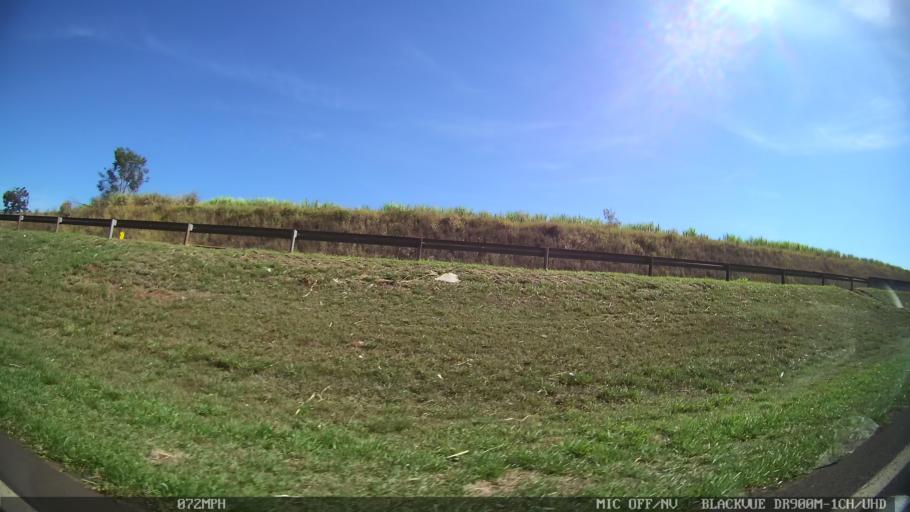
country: BR
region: Sao Paulo
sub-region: Sao Simao
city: Sao Simao
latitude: -21.4985
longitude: -47.6417
